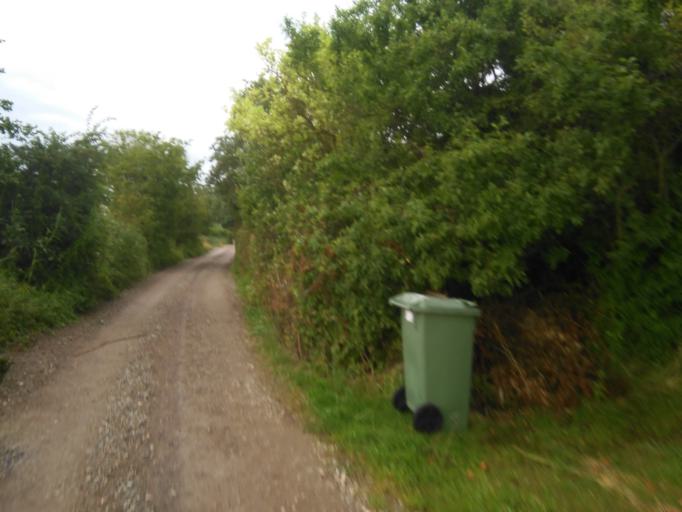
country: DK
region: Central Jutland
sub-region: Arhus Kommune
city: Hjortshoj
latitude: 56.2061
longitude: 10.2821
